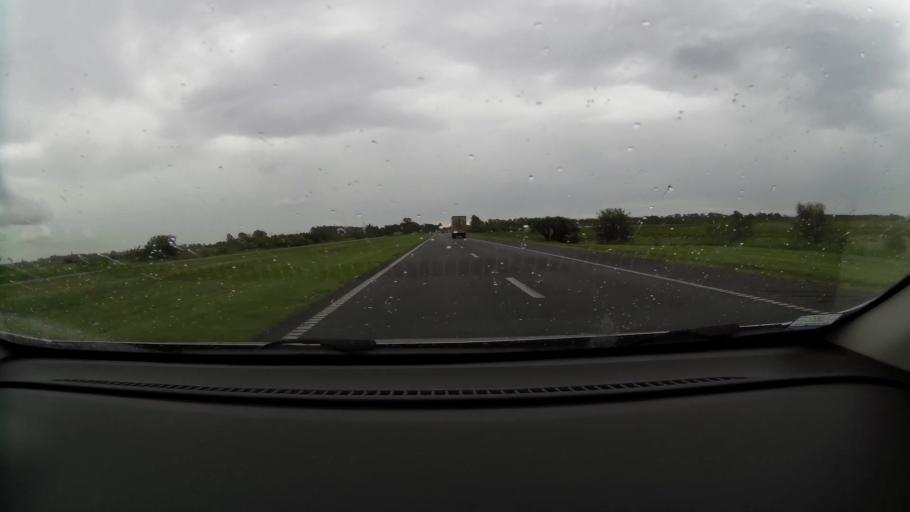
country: AR
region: Buenos Aires
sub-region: Partido de Baradero
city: Baradero
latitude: -33.8056
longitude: -59.6130
